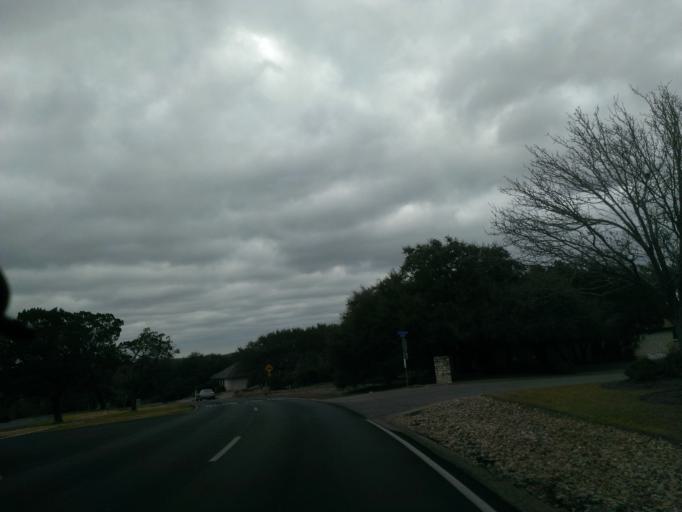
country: US
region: Texas
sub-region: Travis County
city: Lakeway
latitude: 30.3572
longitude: -97.9759
